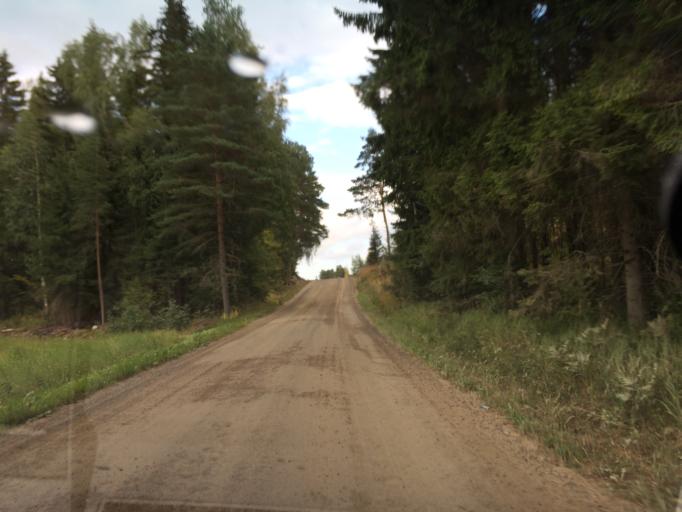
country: FI
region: Pirkanmaa
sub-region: Tampere
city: Luopioinen
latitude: 61.2618
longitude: 24.7031
